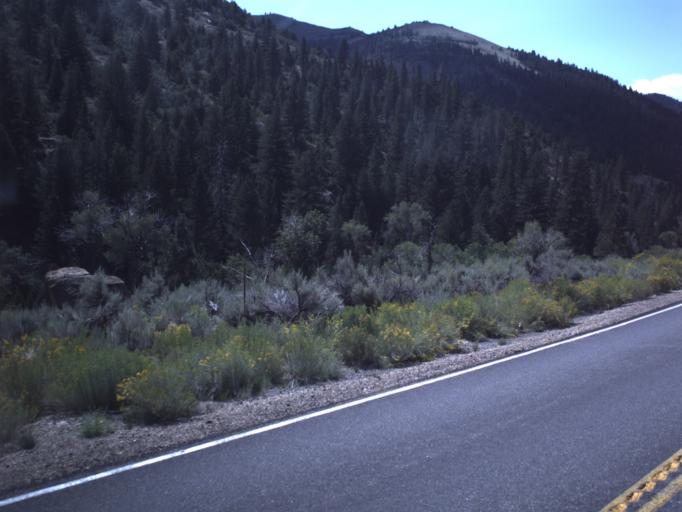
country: US
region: Utah
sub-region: Carbon County
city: Helper
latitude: 39.7748
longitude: -110.8003
